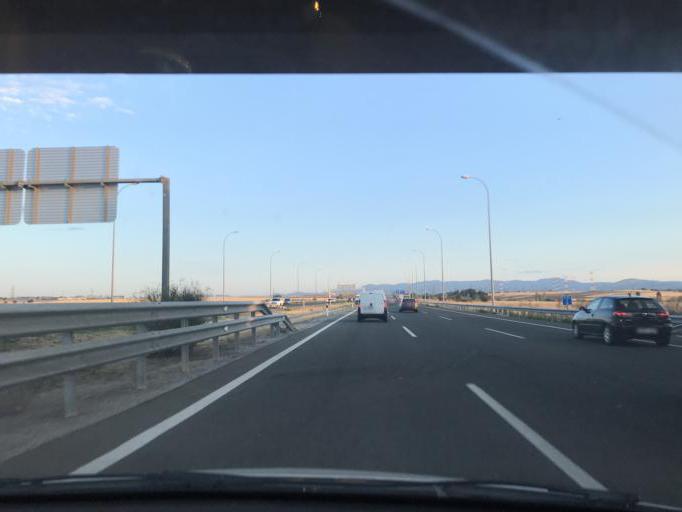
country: ES
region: Madrid
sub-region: Provincia de Madrid
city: San Sebastian de los Reyes
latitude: 40.5496
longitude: -3.5778
